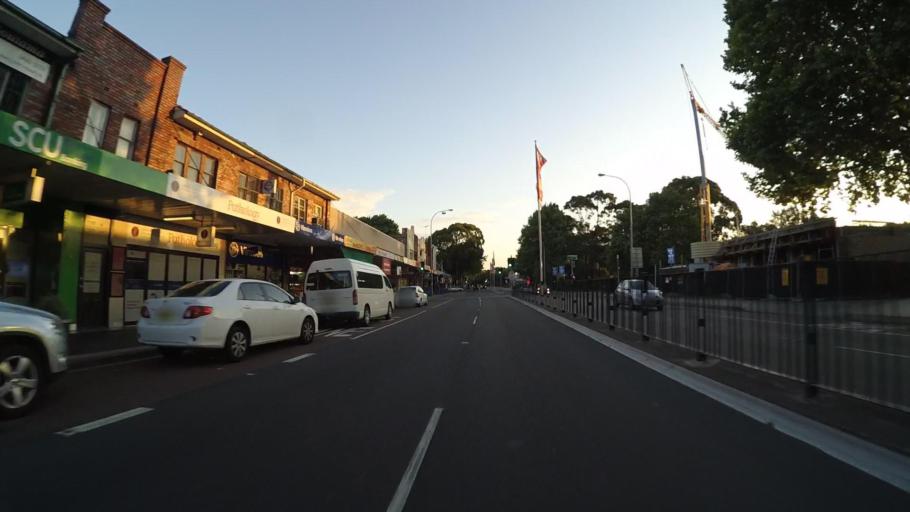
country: AU
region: New South Wales
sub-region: Botany Bay
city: Mascot
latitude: -33.9314
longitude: 151.1941
